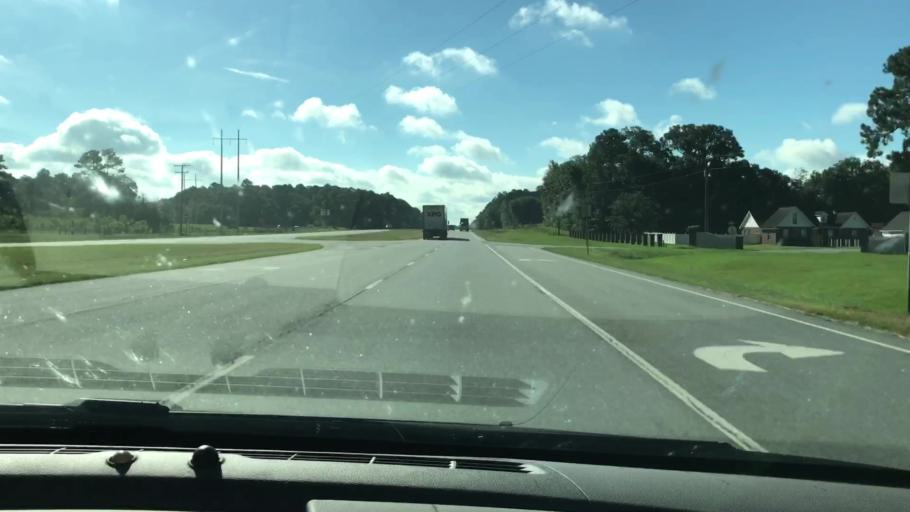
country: US
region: Georgia
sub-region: Dougherty County
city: Albany
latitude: 31.5696
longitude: -84.0223
